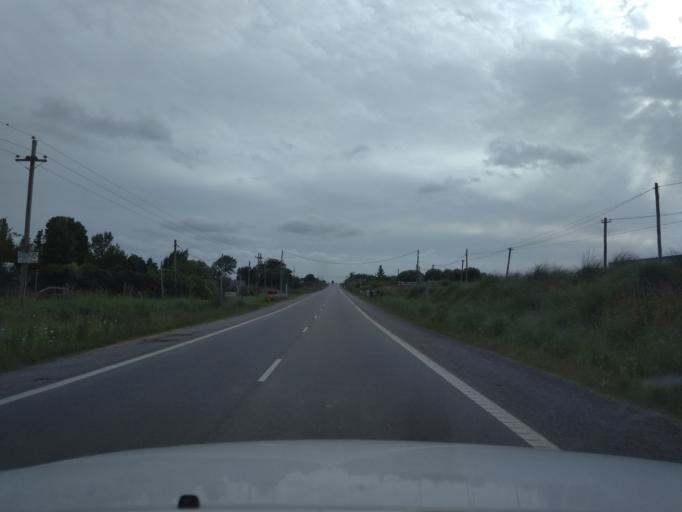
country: UY
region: Canelones
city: Joaquin Suarez
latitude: -34.6959
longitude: -56.0344
